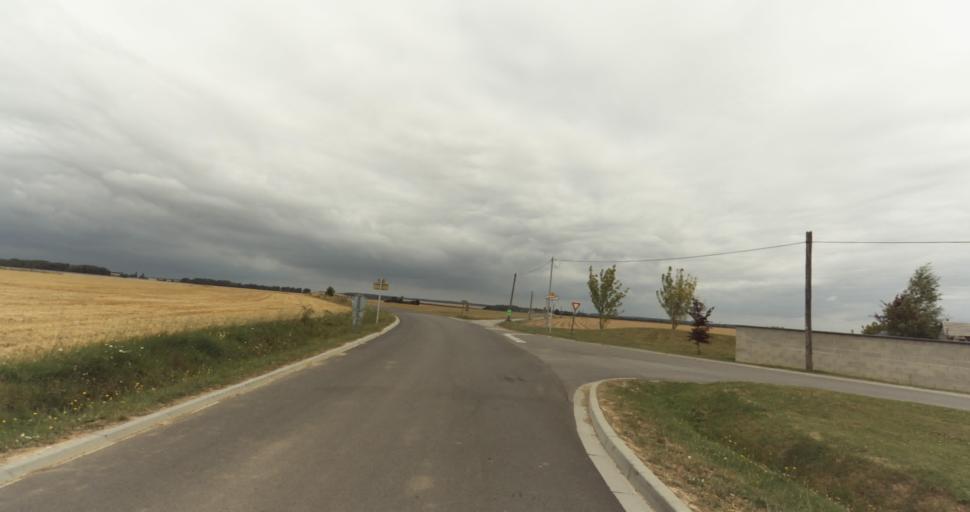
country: FR
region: Haute-Normandie
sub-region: Departement de l'Eure
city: Gravigny
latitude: 49.0346
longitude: 1.2398
